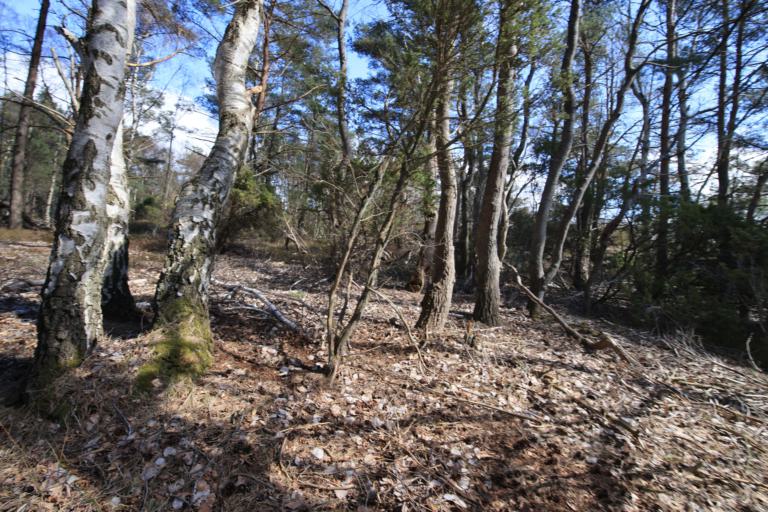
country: SE
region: Halland
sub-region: Varbergs Kommun
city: Varberg
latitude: 57.1733
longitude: 12.2359
